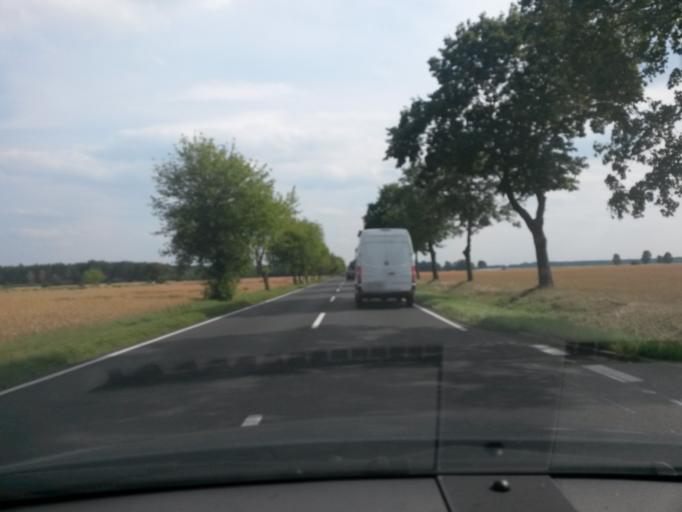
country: PL
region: Greater Poland Voivodeship
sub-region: Powiat sremski
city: Srem
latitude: 52.1454
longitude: 17.0374
